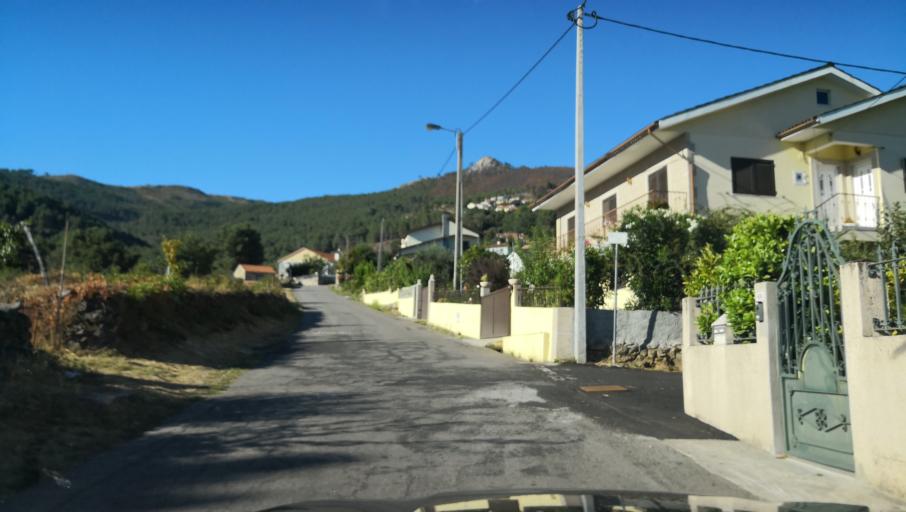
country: PT
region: Vila Real
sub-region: Vila Real
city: Vila Real
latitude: 41.3248
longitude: -7.7690
